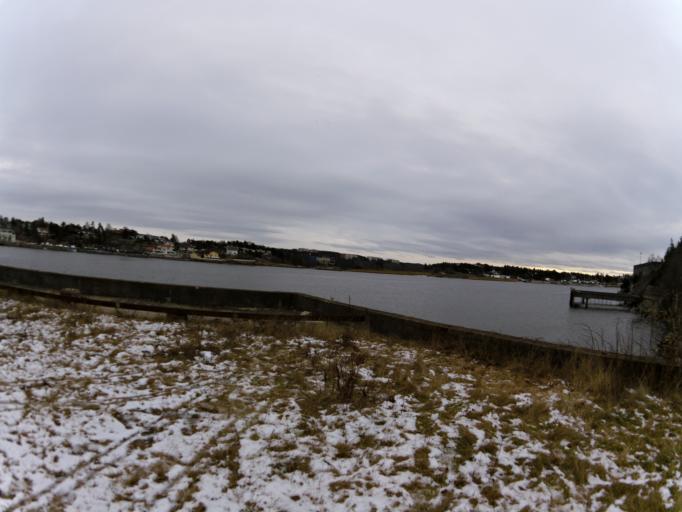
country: NO
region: Ostfold
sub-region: Fredrikstad
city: Fredrikstad
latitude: 59.2006
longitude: 10.8964
